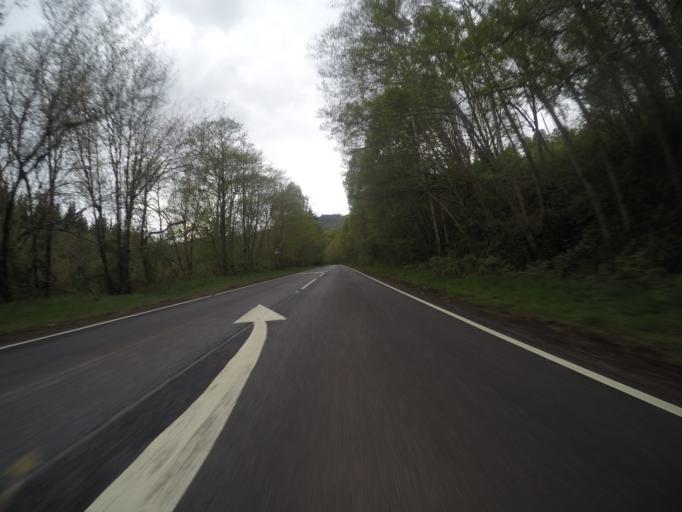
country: GB
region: Scotland
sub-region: Highland
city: Beauly
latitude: 57.2212
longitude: -4.6382
